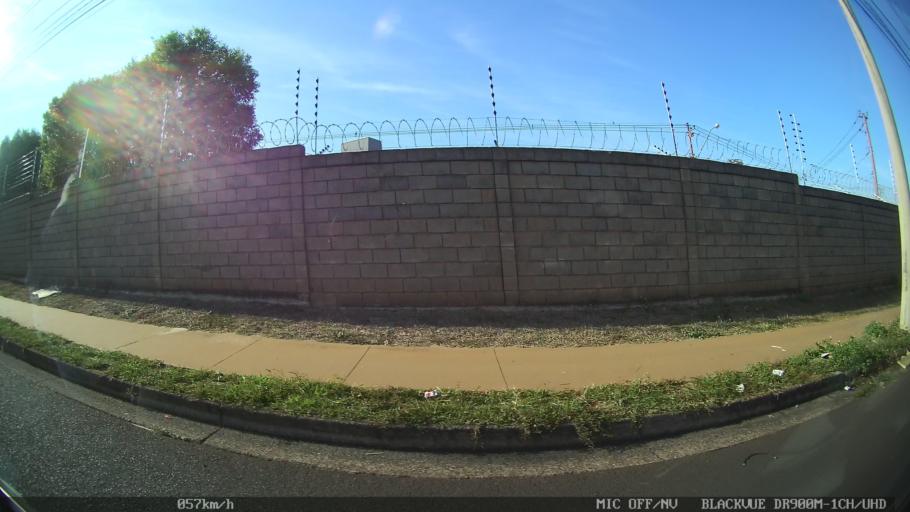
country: BR
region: Sao Paulo
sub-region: Sao Jose Do Rio Preto
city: Sao Jose do Rio Preto
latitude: -20.7775
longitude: -49.3419
